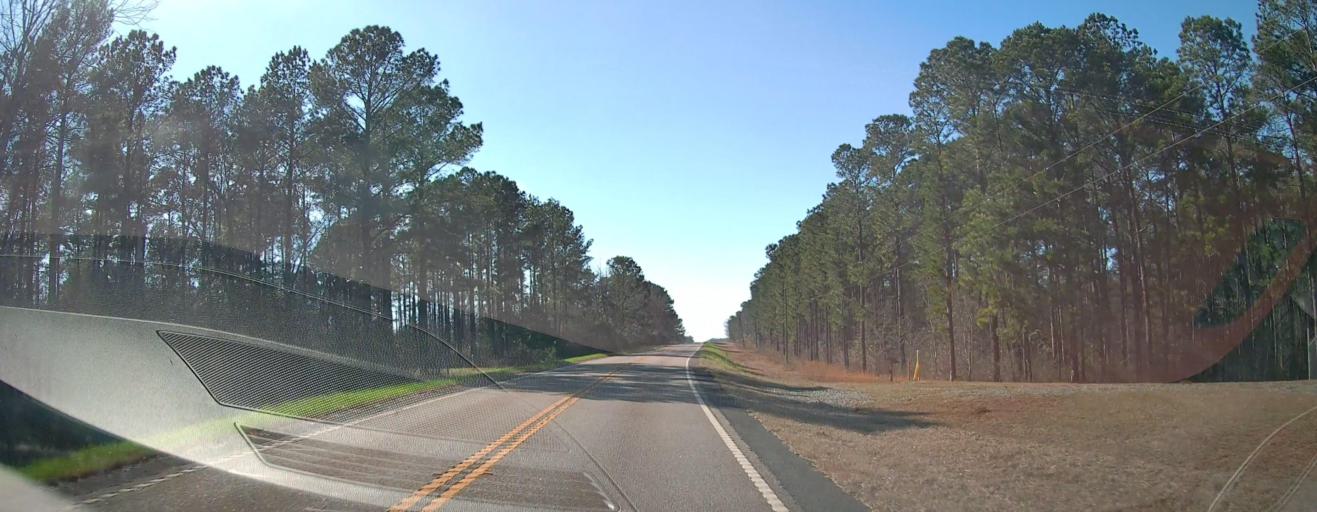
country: US
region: Georgia
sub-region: Sumter County
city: Americus
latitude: 32.1880
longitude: -84.1673
